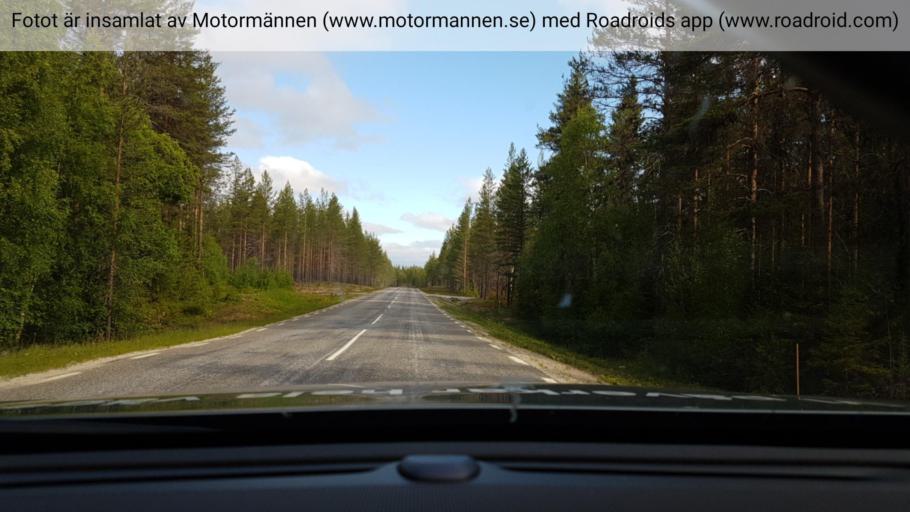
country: SE
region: Vaesterbotten
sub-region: Norsjo Kommun
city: Norsjoe
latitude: 64.7296
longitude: 19.1320
